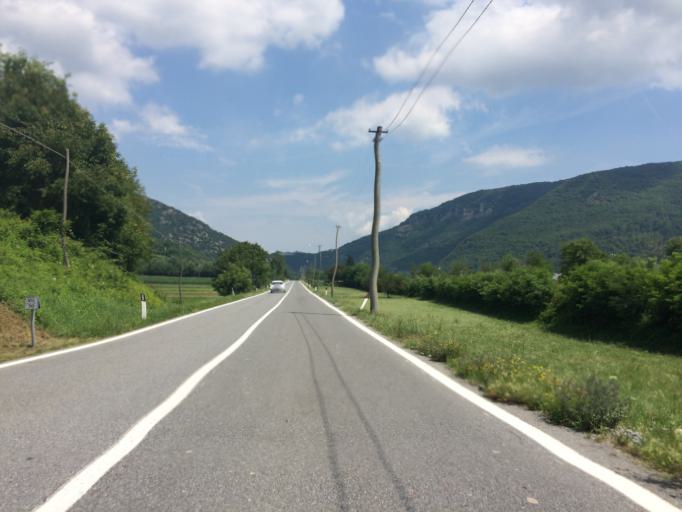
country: IT
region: Piedmont
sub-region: Provincia di Cuneo
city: Priola
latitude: 44.2597
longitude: 8.0236
